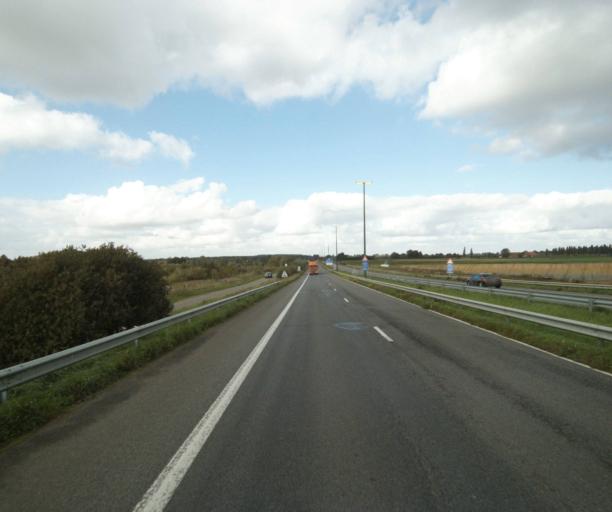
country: FR
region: Nord-Pas-de-Calais
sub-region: Departement du Nord
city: Frelinghien
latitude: 50.7154
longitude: 2.9141
